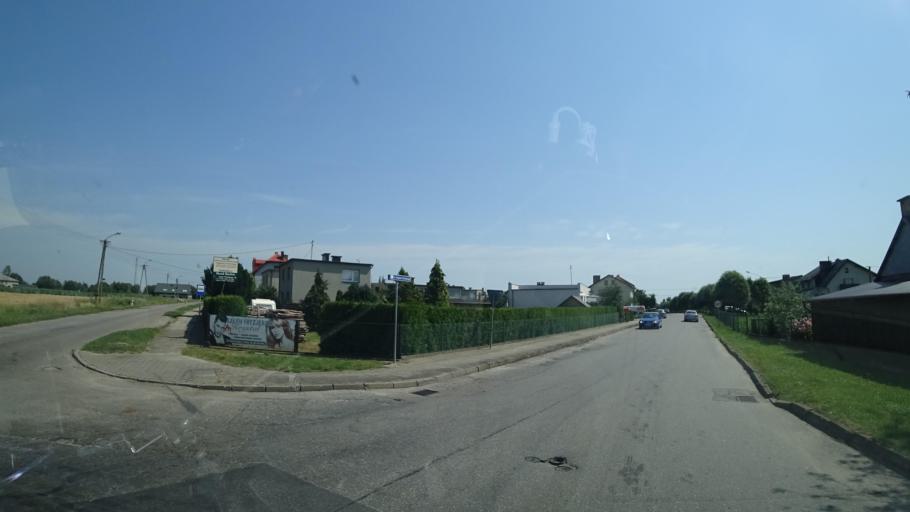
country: PL
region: Pomeranian Voivodeship
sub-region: Powiat chojnicki
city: Brusy
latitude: 53.8848
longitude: 17.7073
